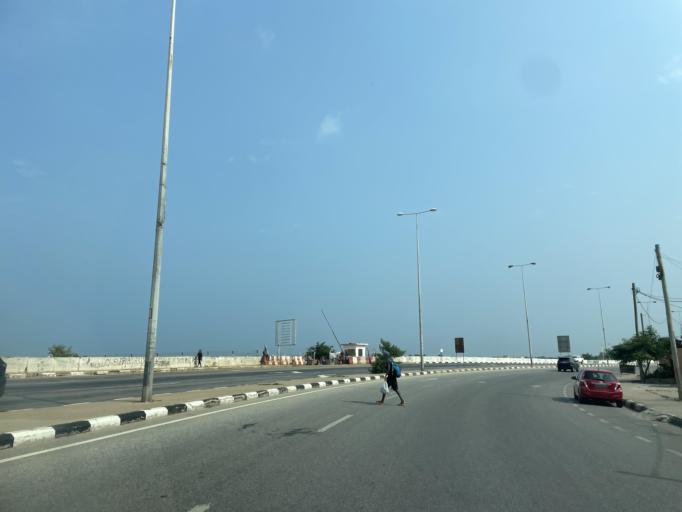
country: AO
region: Luanda
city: Luanda
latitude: -8.8284
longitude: 13.2141
